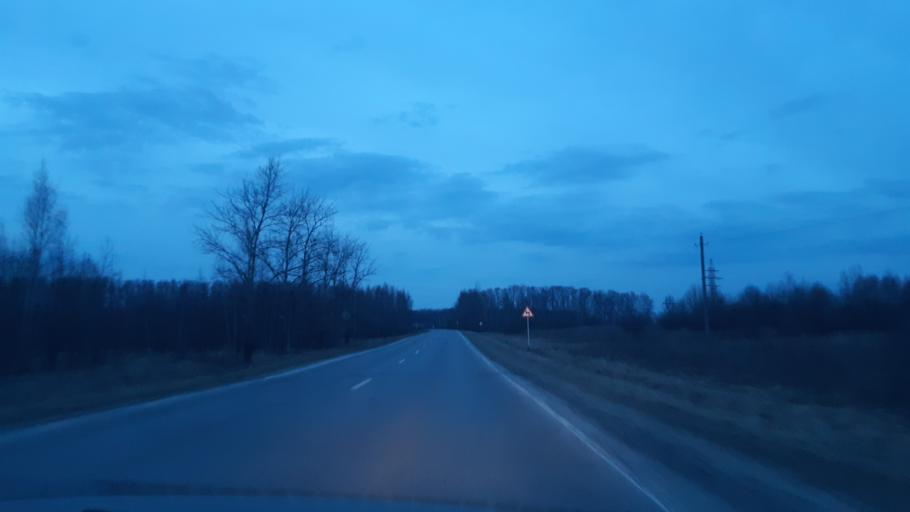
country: RU
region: Vladimir
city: Luknovo
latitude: 56.2187
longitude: 42.0323
